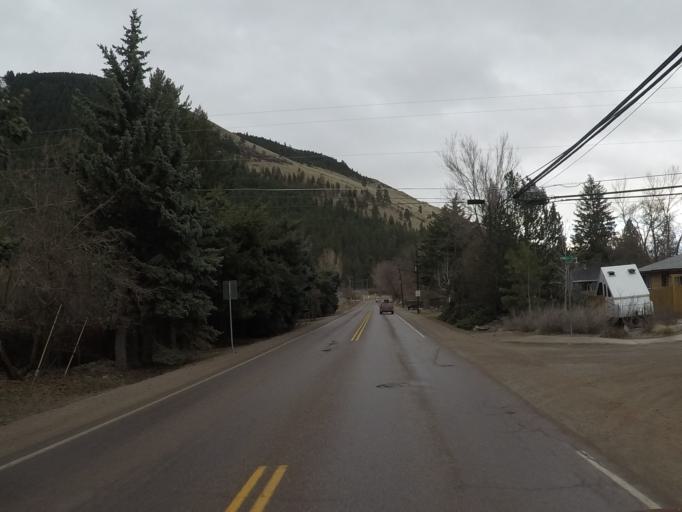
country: US
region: Montana
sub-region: Missoula County
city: East Missoula
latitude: 46.8872
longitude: -113.9657
